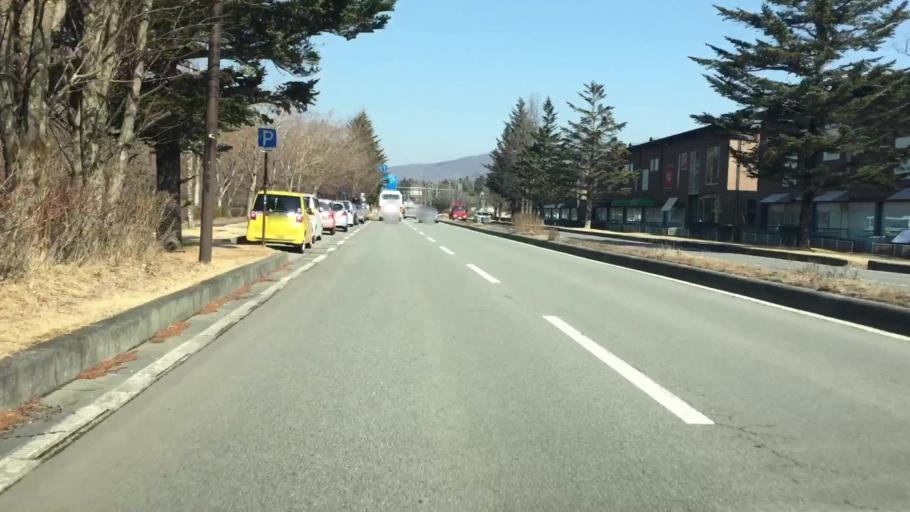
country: JP
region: Nagano
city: Saku
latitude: 36.3394
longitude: 138.6309
